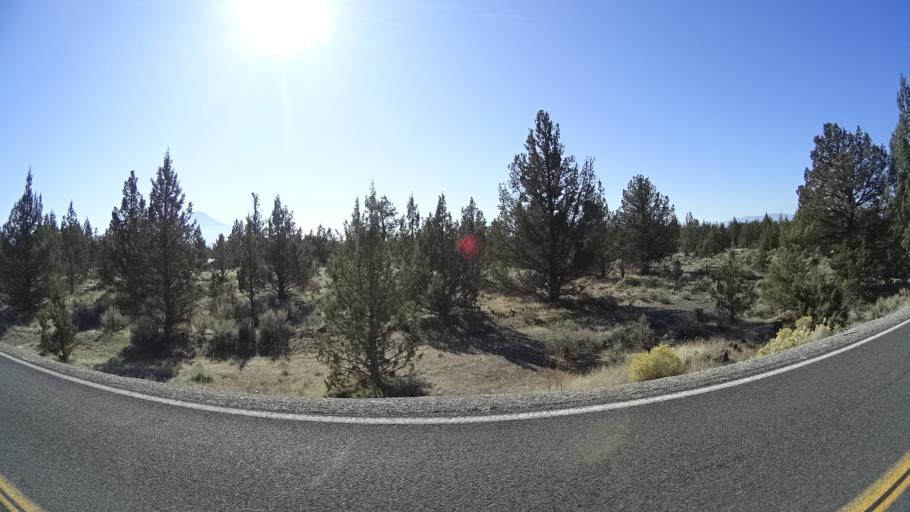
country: US
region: California
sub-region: Siskiyou County
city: Montague
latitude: 41.6593
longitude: -122.3763
